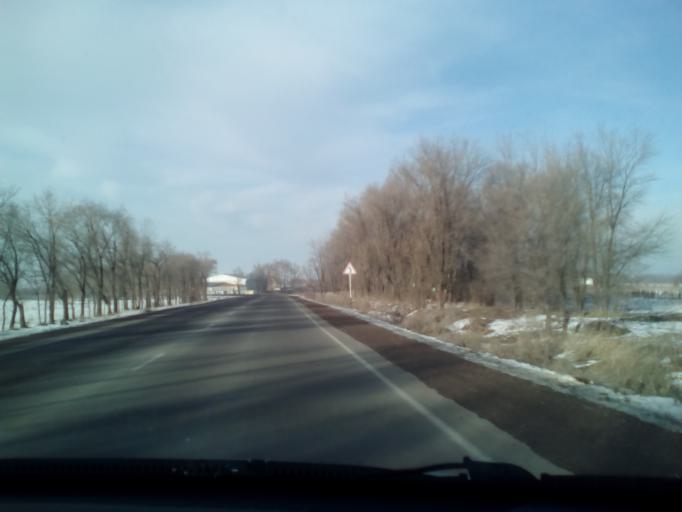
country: KZ
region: Almaty Oblysy
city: Burunday
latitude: 43.2119
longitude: 76.4150
